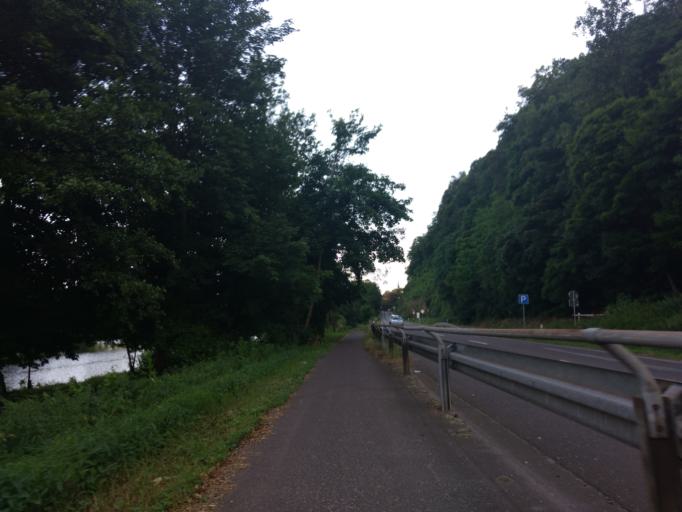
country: DE
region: Saarland
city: Wallerfangen
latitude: 49.3359
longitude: 6.7170
